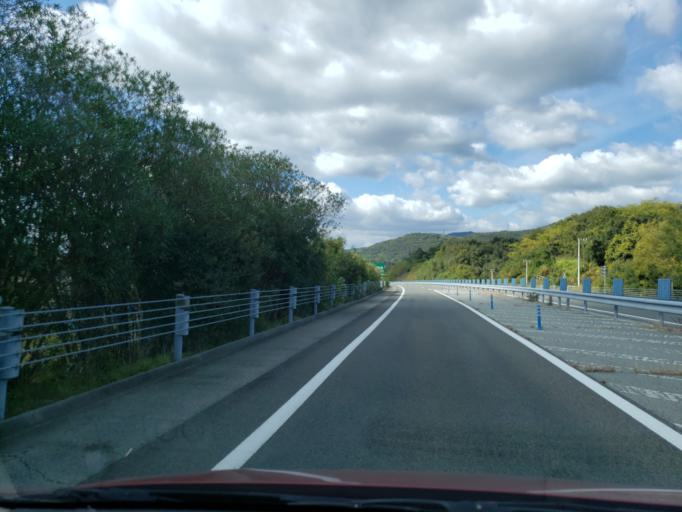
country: JP
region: Tokushima
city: Kamojimacho-jogejima
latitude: 34.1221
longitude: 134.3646
